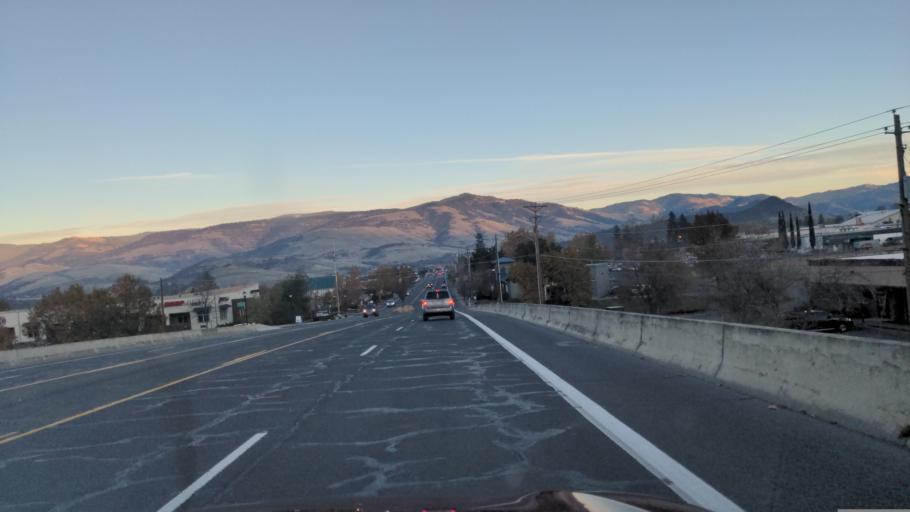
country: US
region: Oregon
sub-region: Jackson County
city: Ashland
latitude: 42.1853
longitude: -122.6758
